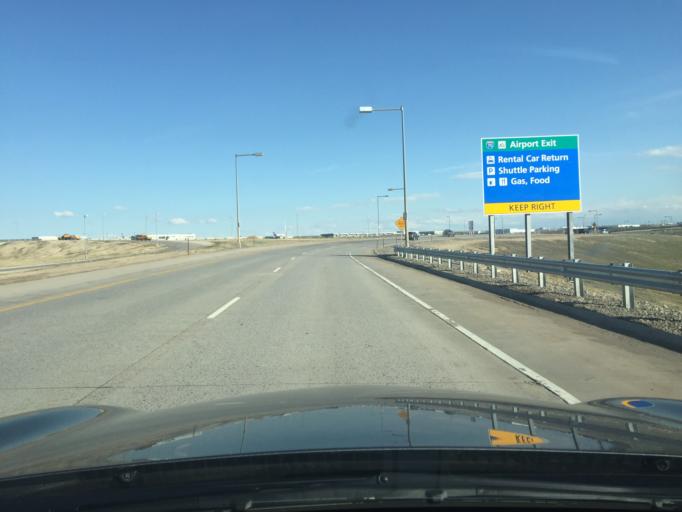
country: US
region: Colorado
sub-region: Weld County
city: Lochbuie
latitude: 39.8428
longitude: -104.6772
